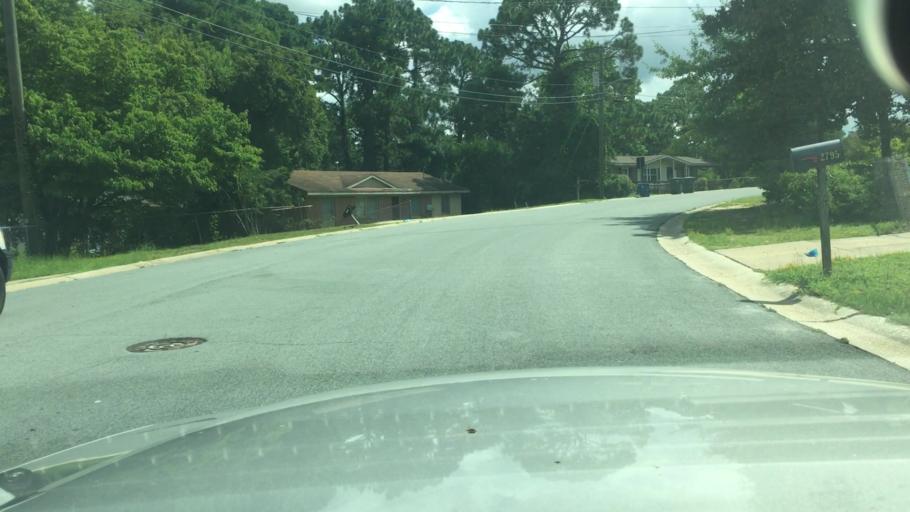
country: US
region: North Carolina
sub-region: Cumberland County
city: Fayetteville
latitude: 35.0262
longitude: -78.9174
